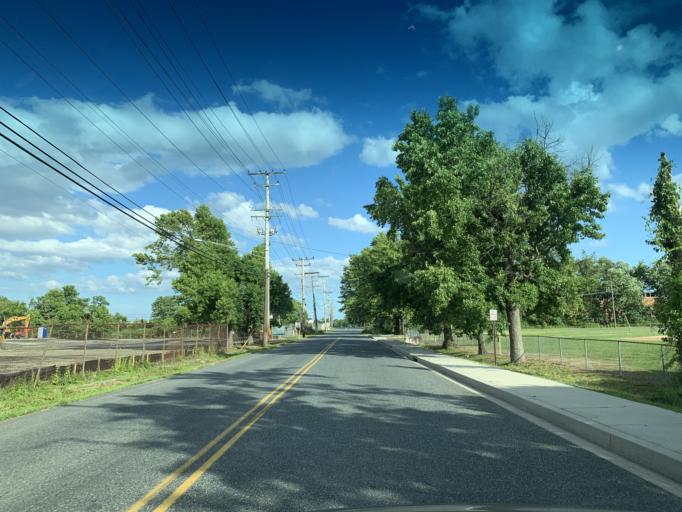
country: US
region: Maryland
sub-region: Harford County
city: Havre de Grace
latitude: 39.5366
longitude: -76.1116
